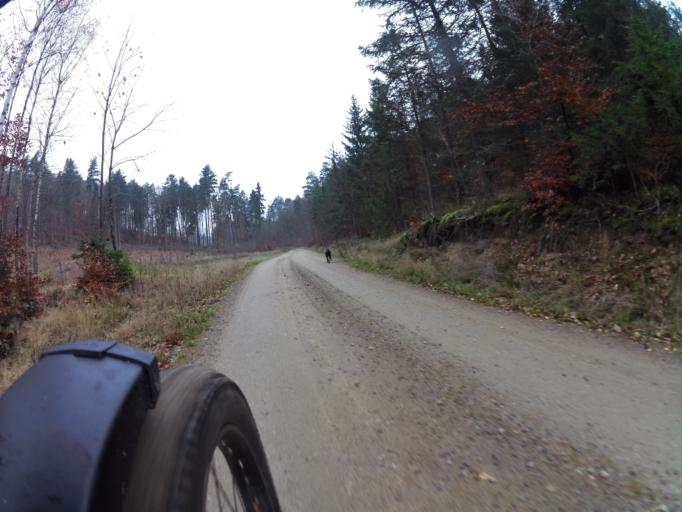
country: PL
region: Pomeranian Voivodeship
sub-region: Powiat pucki
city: Krokowa
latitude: 54.7097
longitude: 18.1453
